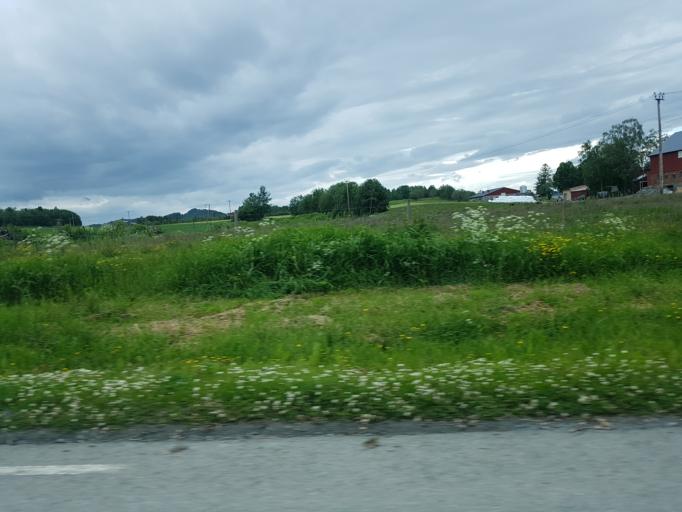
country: NO
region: Nord-Trondelag
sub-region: Levanger
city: Skogn
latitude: 63.6102
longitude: 11.0772
